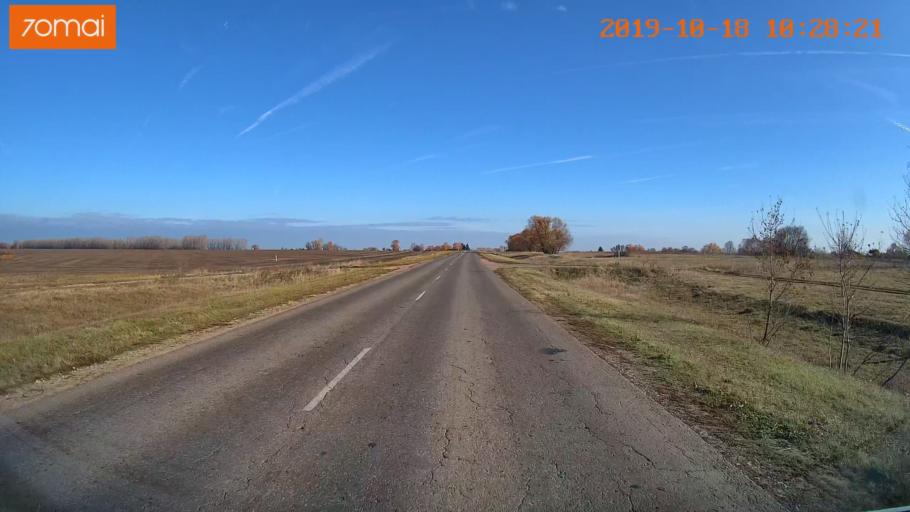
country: RU
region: Tula
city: Kurkino
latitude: 53.4430
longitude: 38.6535
